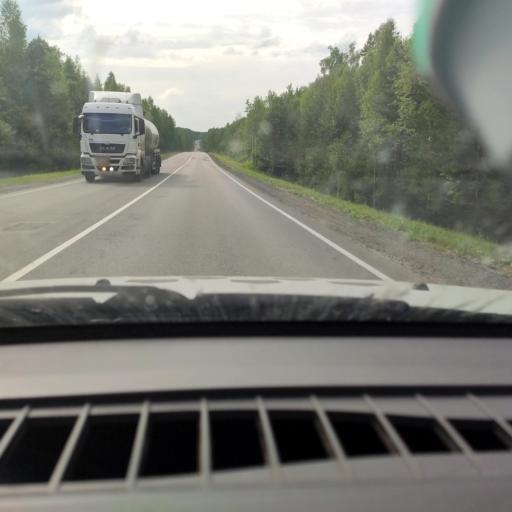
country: RU
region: Kirov
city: Chernaya Kholunitsa
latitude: 58.8631
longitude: 51.5954
